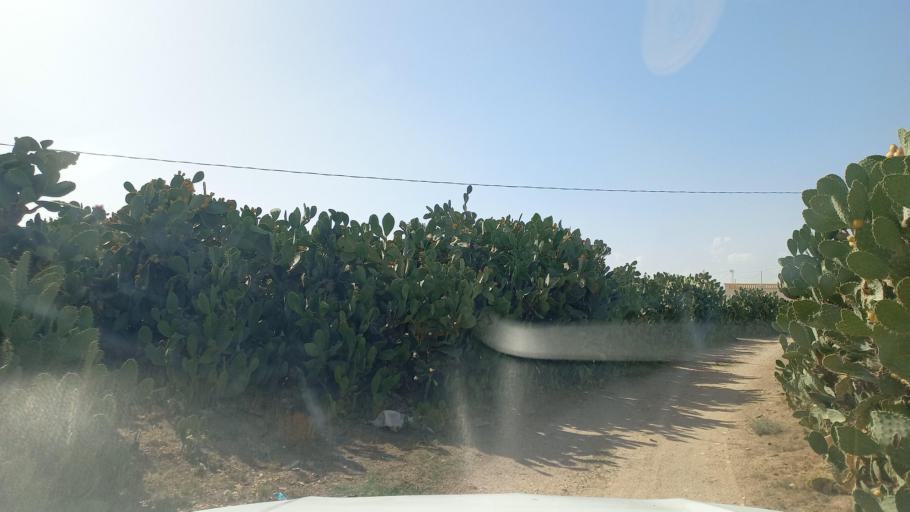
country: TN
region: Al Qasrayn
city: Sbiba
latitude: 35.3041
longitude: 9.0406
